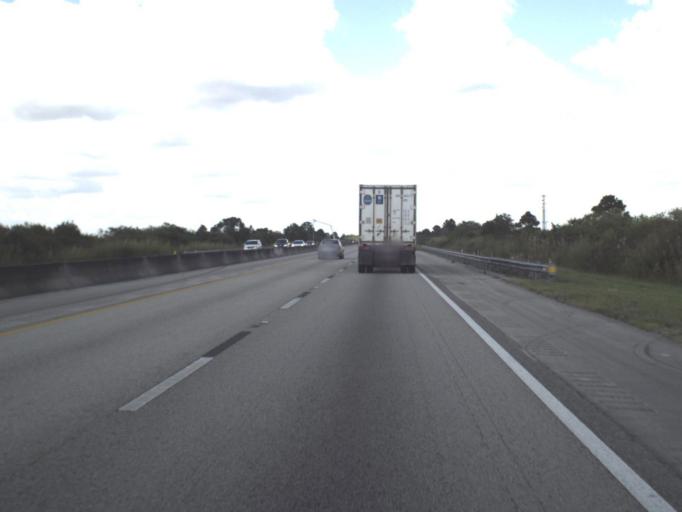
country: US
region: Florida
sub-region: Palm Beach County
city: Tequesta
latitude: 27.0061
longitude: -80.2092
